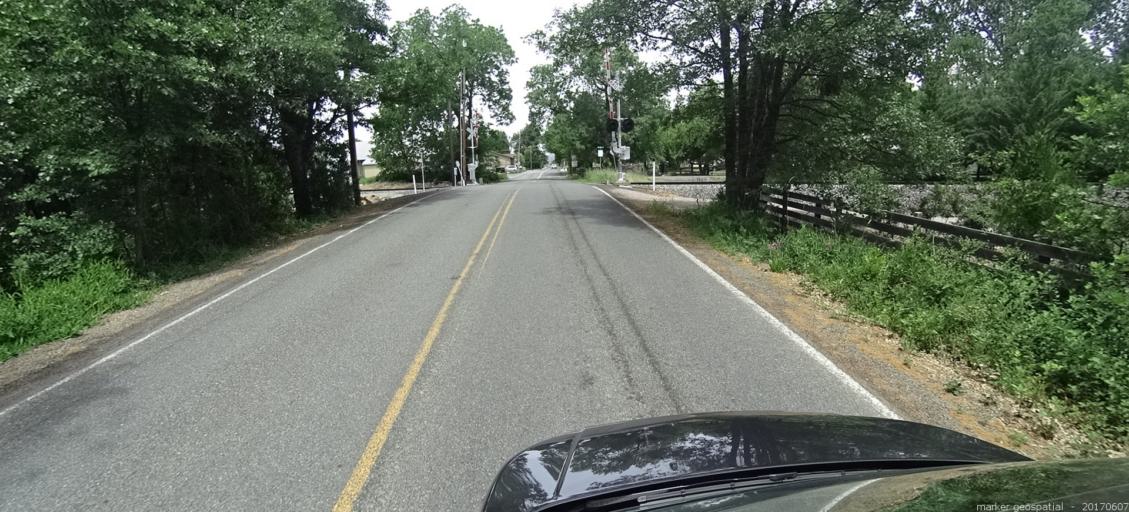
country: US
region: California
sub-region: Siskiyou County
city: Mount Shasta
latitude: 41.3019
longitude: -122.3112
